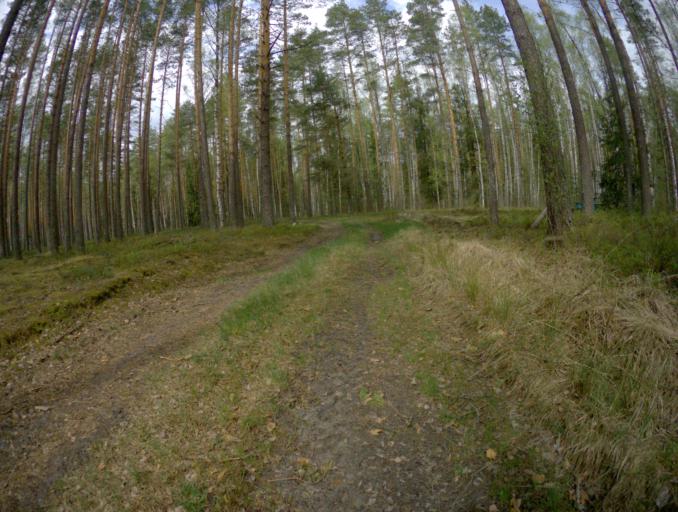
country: RU
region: Vladimir
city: Golovino
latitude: 55.9297
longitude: 40.3783
